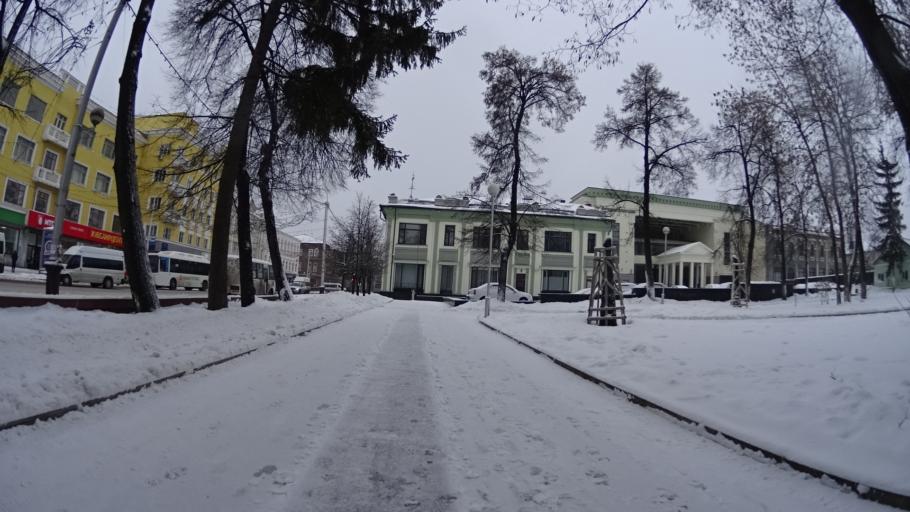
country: RU
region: Bashkortostan
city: Ufa
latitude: 54.7255
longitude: 55.9469
